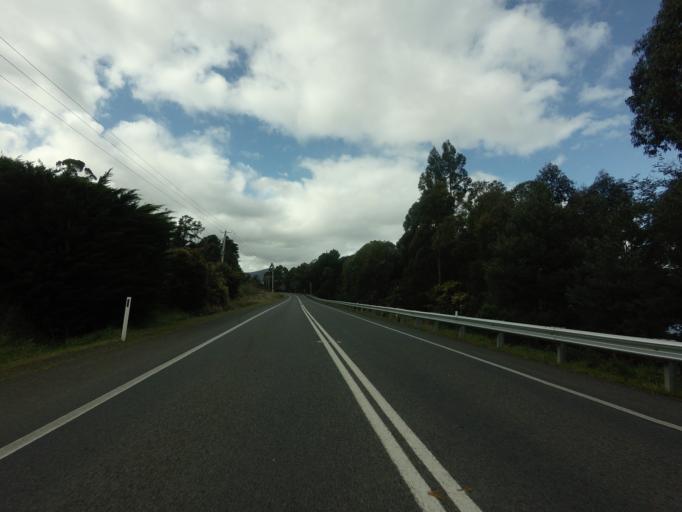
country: AU
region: Tasmania
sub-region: Huon Valley
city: Franklin
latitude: -43.1109
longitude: 146.9983
